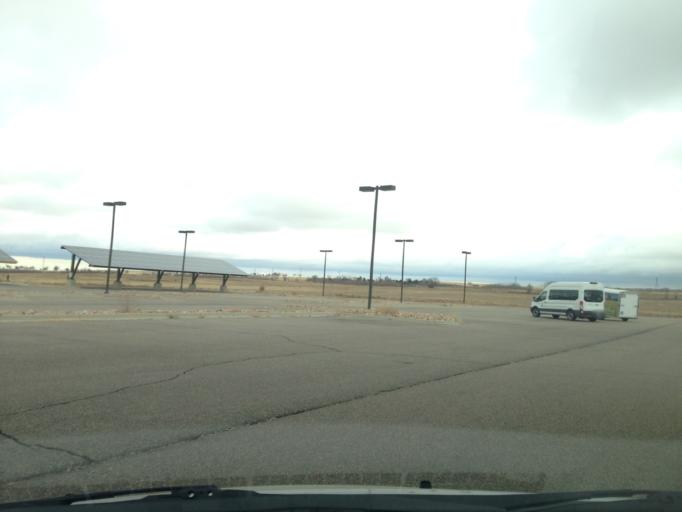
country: US
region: Colorado
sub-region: Adams County
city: Derby
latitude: 39.8140
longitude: -104.8800
